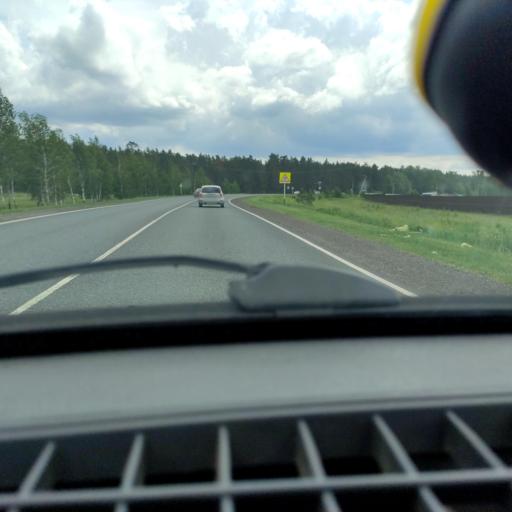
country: RU
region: Samara
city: Povolzhskiy
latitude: 53.6329
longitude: 49.6589
